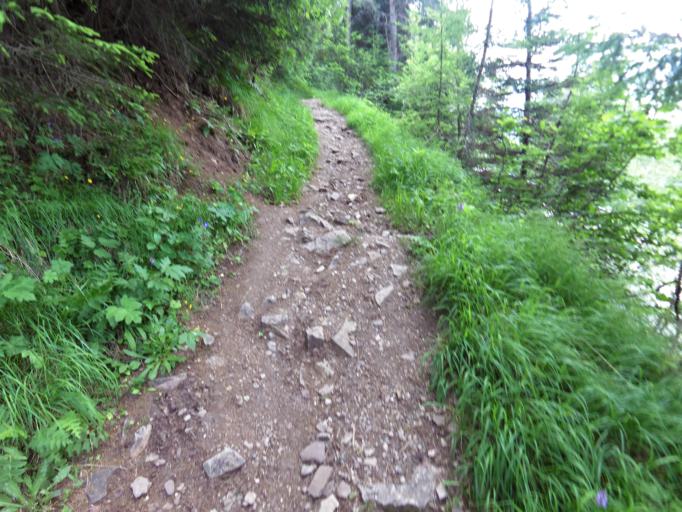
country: IT
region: Trentino-Alto Adige
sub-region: Bolzano
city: Siusi
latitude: 46.5422
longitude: 11.5866
